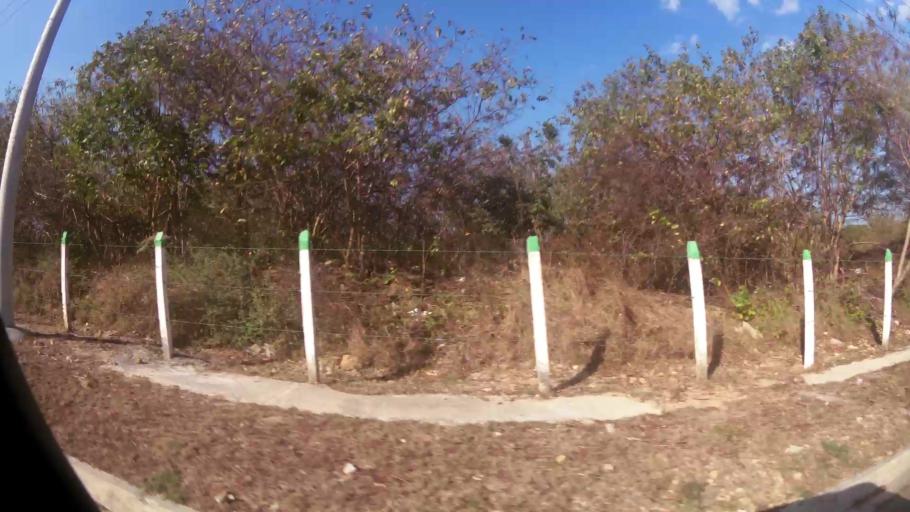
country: CO
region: Atlantico
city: Barranquilla
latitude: 11.0016
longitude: -74.8375
